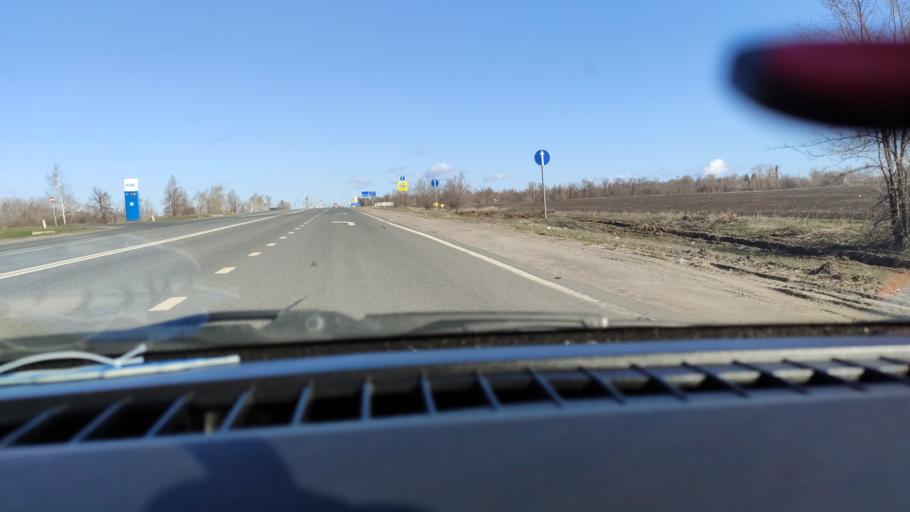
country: RU
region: Samara
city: Syzran'
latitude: 53.2067
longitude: 48.5087
